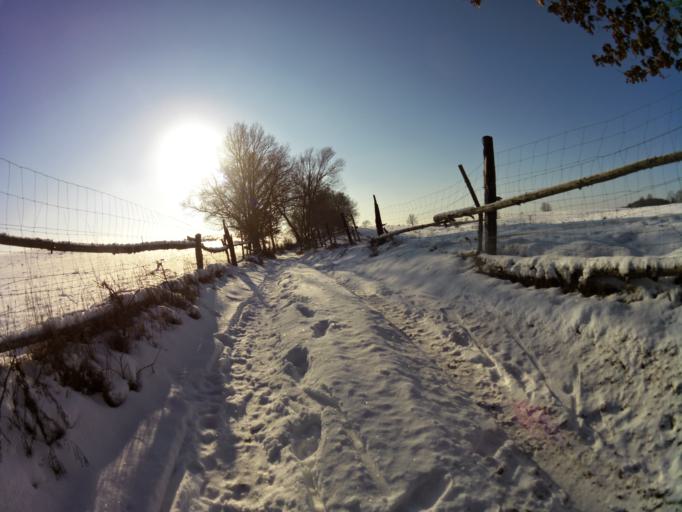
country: PL
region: West Pomeranian Voivodeship
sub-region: Powiat stargardzki
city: Dobrzany
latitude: 53.3856
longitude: 15.4864
